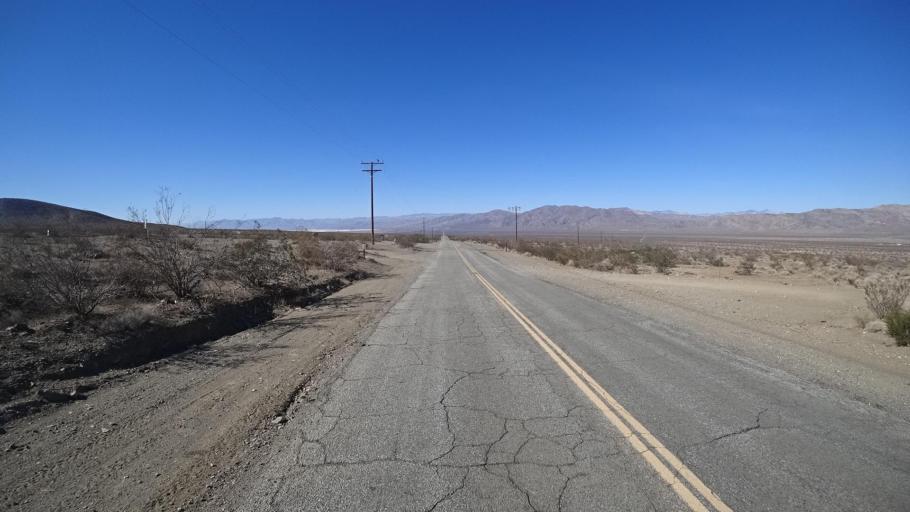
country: US
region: California
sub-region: Kern County
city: Ridgecrest
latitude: 35.3803
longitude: -117.6767
